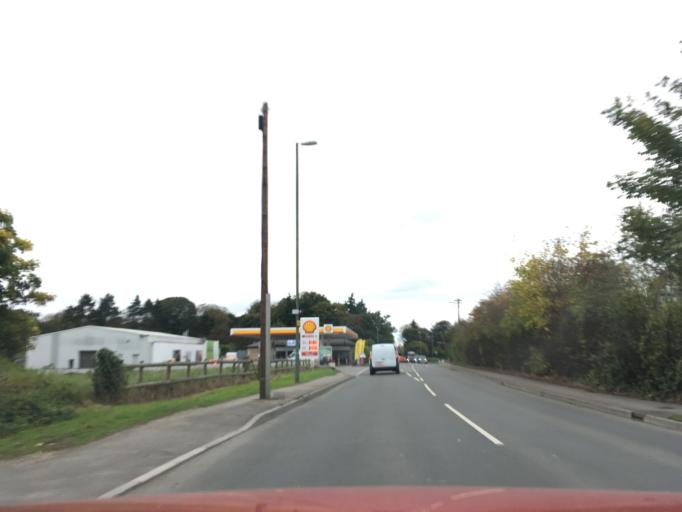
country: GB
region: England
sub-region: Gloucestershire
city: Dursley
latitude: 51.7089
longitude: -2.3655
